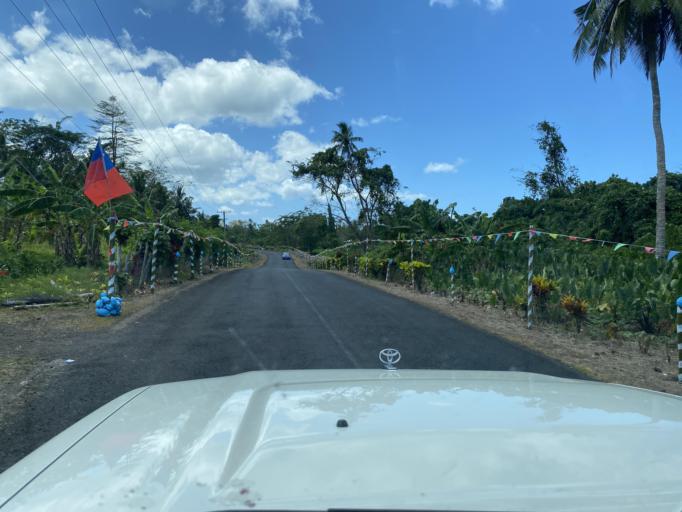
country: WS
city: Lotofaga
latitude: -14.0026
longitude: -171.8150
